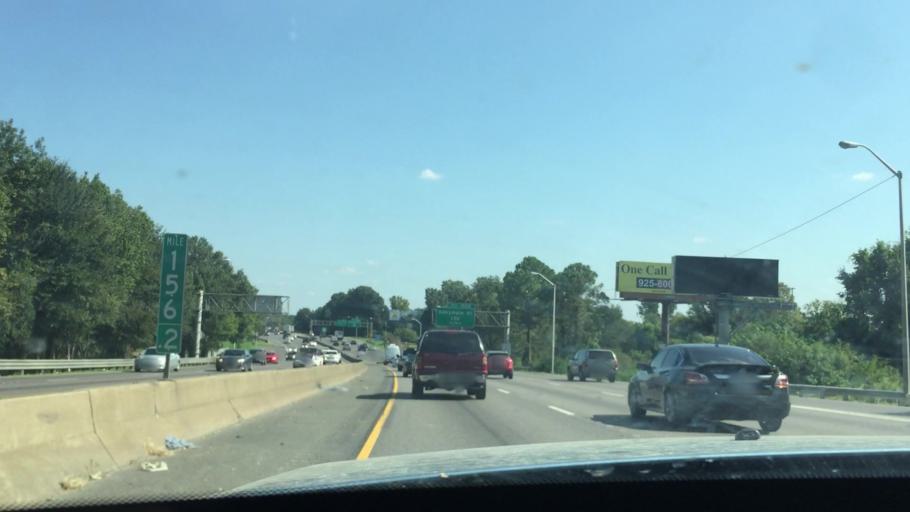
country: US
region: Louisiana
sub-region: East Baton Rouge Parish
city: Baton Rouge
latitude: 30.4304
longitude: -91.1737
